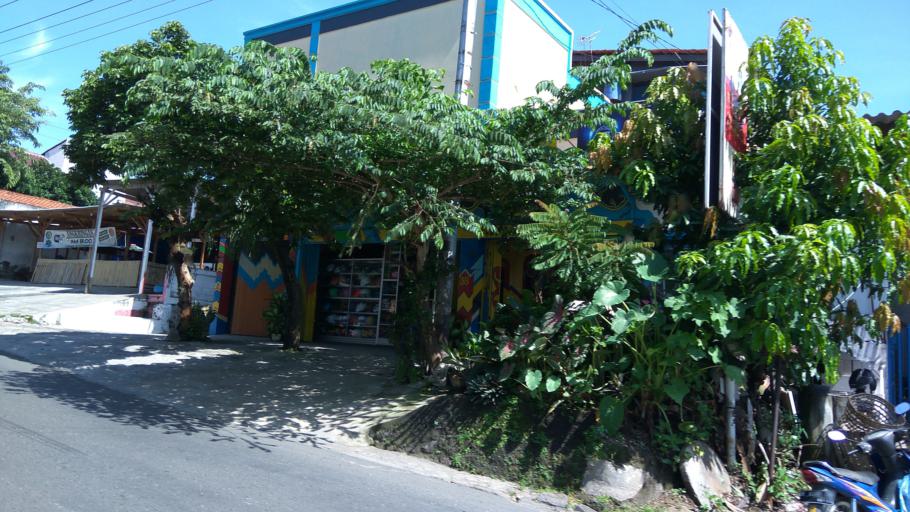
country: ID
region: Central Java
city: Ungaran
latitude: -7.0751
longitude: 110.4161
